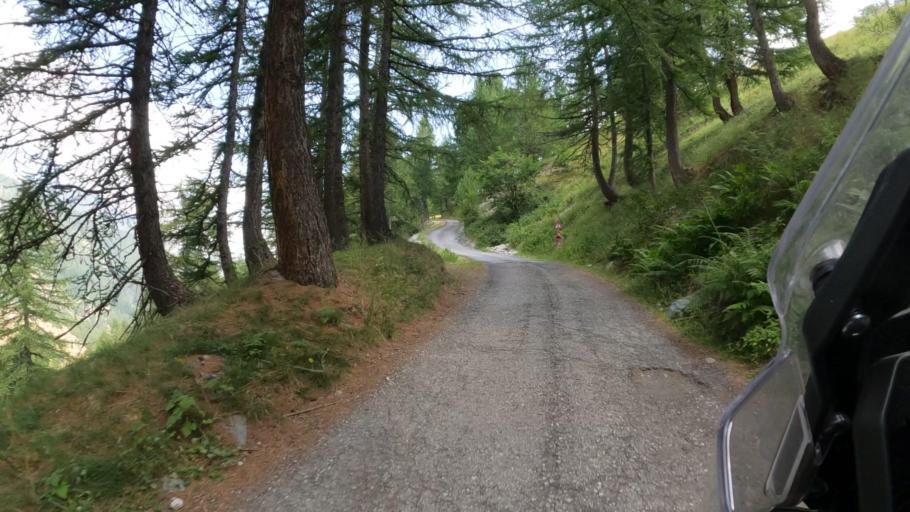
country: IT
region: Piedmont
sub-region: Provincia di Cuneo
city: Marmora
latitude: 44.4177
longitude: 7.1046
